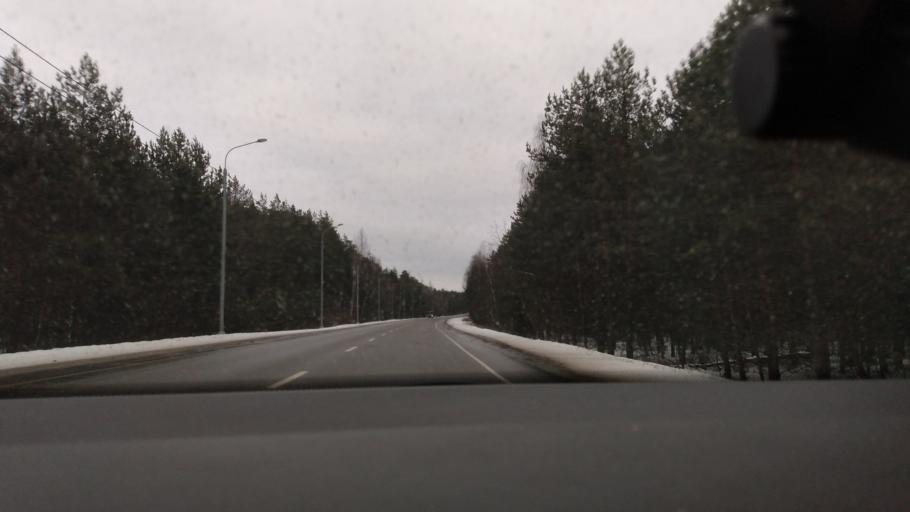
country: RU
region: Moskovskaya
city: Il'inskiy Pogost
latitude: 55.4755
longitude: 38.9506
